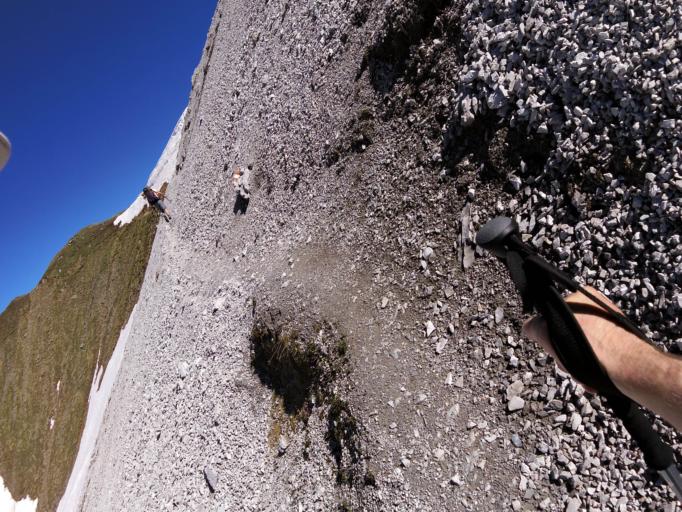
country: AT
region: Tyrol
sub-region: Politischer Bezirk Innsbruck Land
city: Neustift im Stubaital
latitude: 47.1442
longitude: 11.2687
